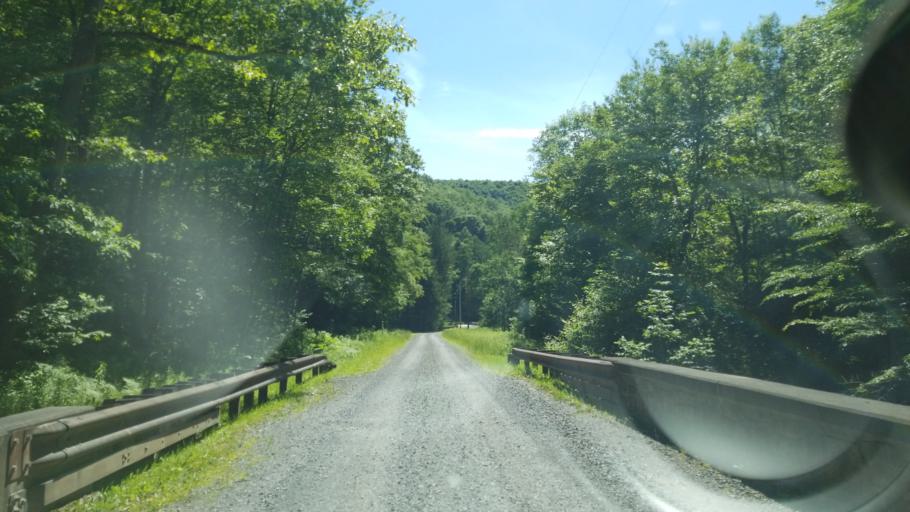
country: US
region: Pennsylvania
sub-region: Clearfield County
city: Clearfield
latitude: 41.2212
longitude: -78.3896
